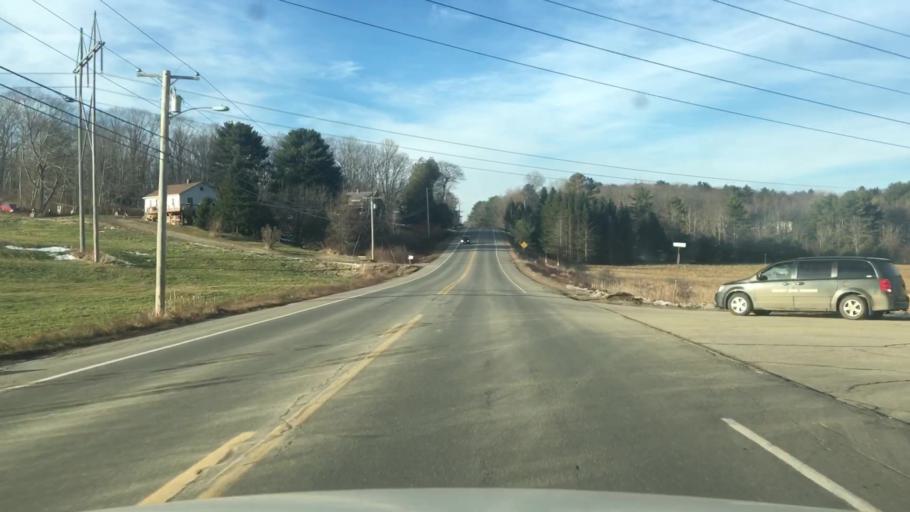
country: US
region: Maine
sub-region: Lincoln County
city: Wiscasset
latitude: 44.0430
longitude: -69.6762
